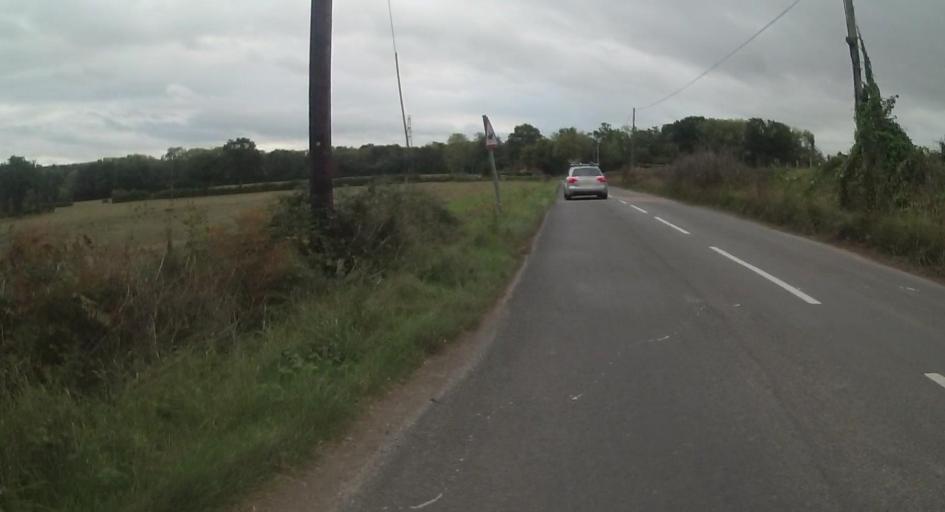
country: GB
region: England
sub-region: Hampshire
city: Fleet
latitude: 51.2560
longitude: -0.8660
